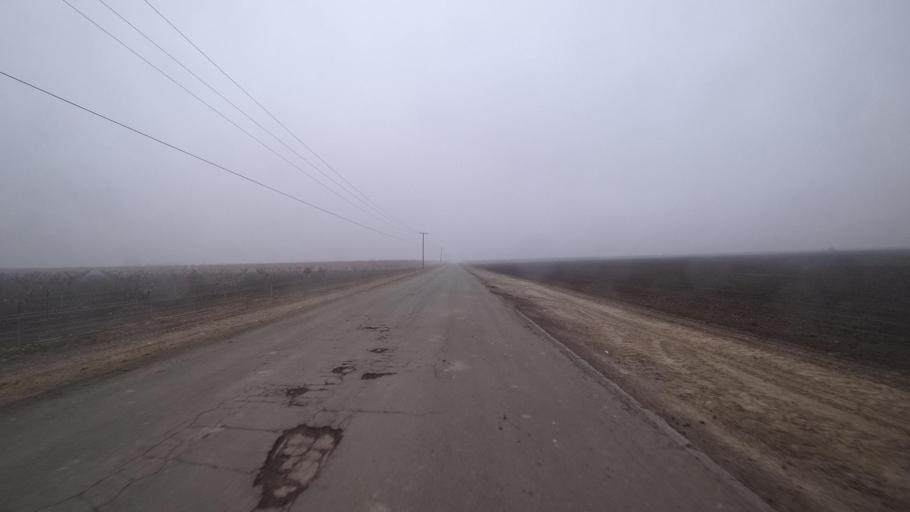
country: US
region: California
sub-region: Kern County
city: Buttonwillow
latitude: 35.4468
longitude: -119.5177
